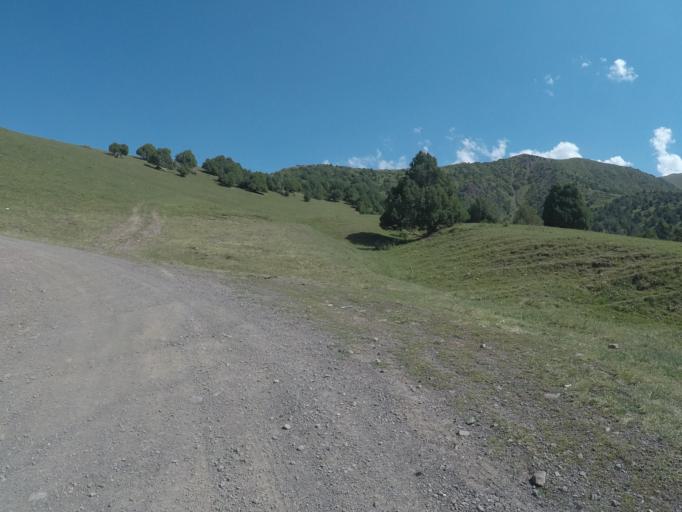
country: KG
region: Chuy
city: Bishkek
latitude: 42.6470
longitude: 74.5557
